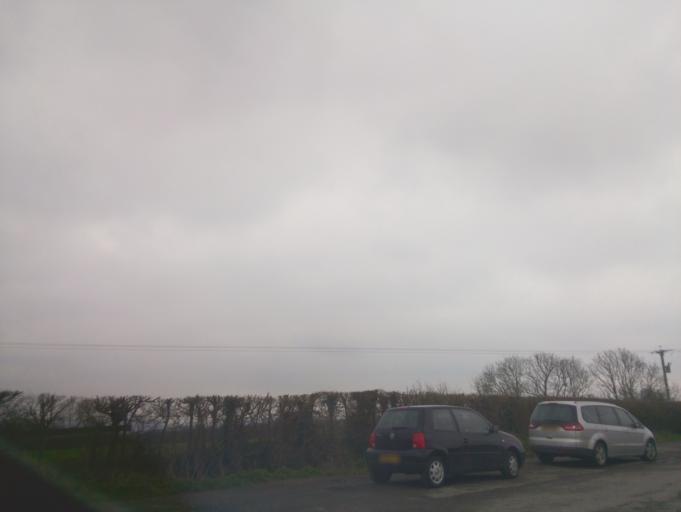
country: GB
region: England
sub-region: South Gloucestershire
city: Charfield
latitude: 51.6286
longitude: -2.4194
